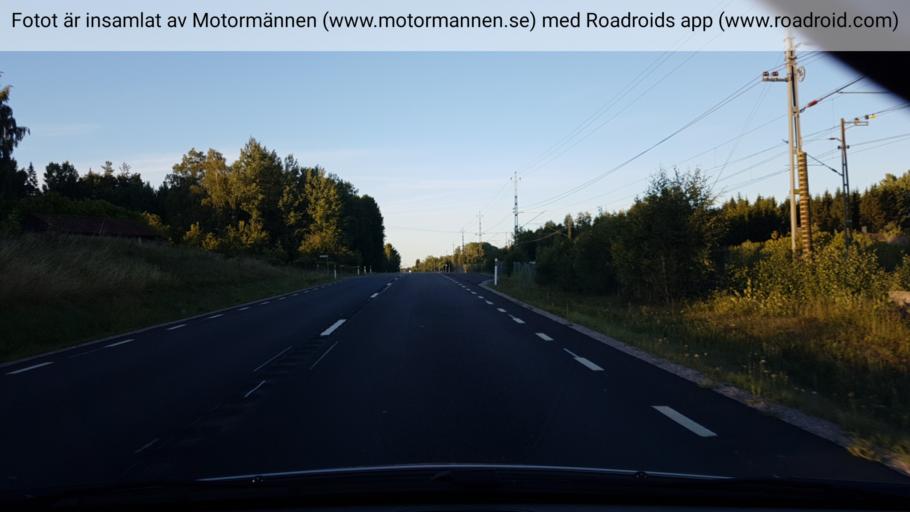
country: SE
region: Vaestmanland
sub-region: Kopings Kommun
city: Koping
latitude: 59.4354
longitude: 15.9396
